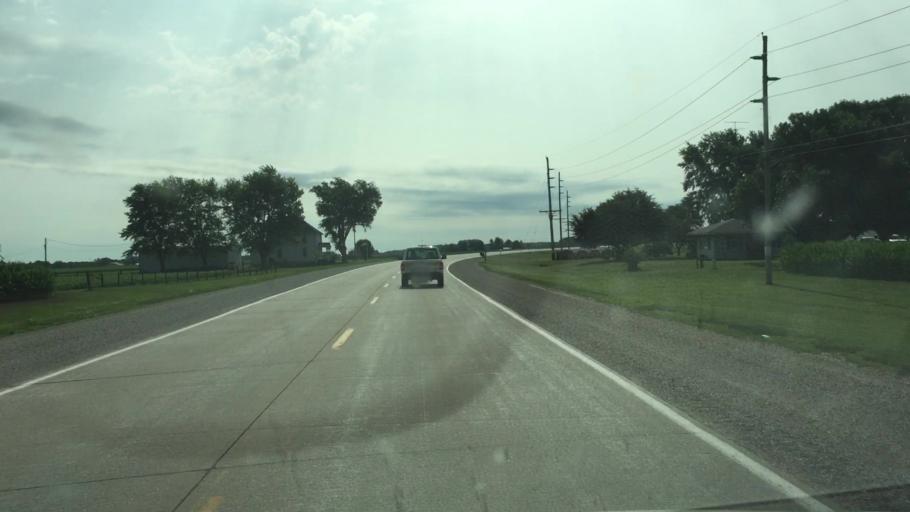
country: US
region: Illinois
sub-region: Hancock County
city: Nauvoo
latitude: 40.6391
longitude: -91.5271
